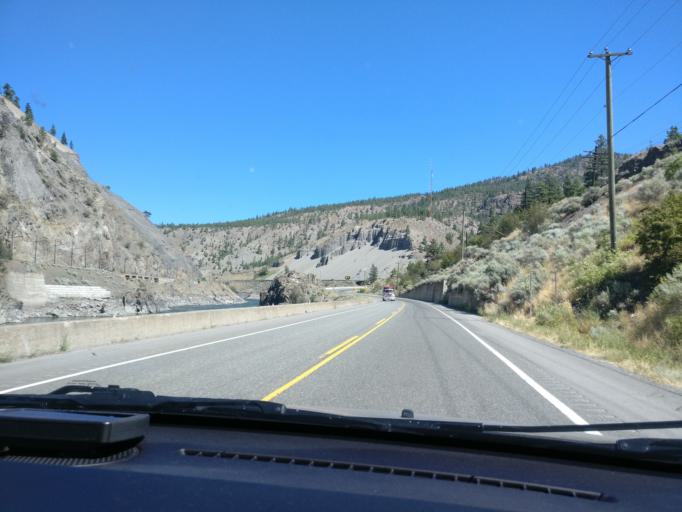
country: CA
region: British Columbia
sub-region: Thompson-Nicola Regional District
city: Ashcroft
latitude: 50.2649
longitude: -121.4046
